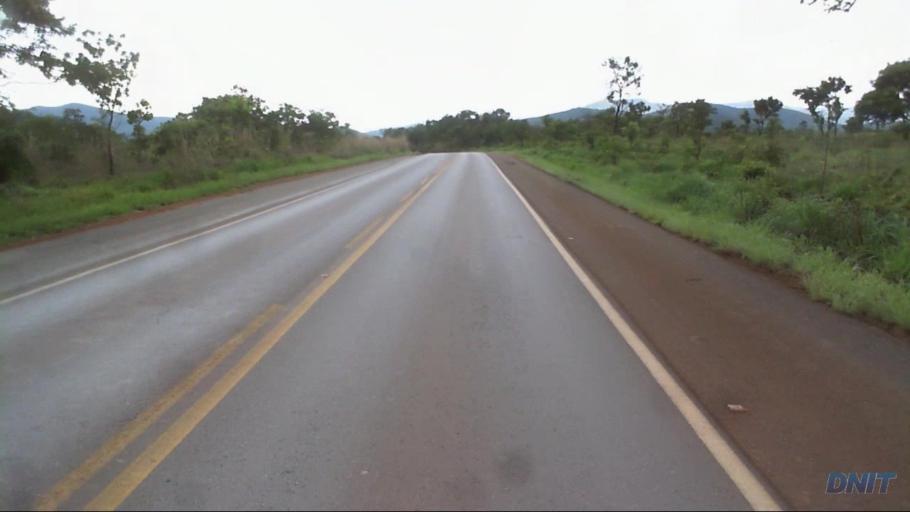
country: BR
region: Goias
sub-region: Barro Alto
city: Barro Alto
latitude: -14.8644
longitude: -49.0170
